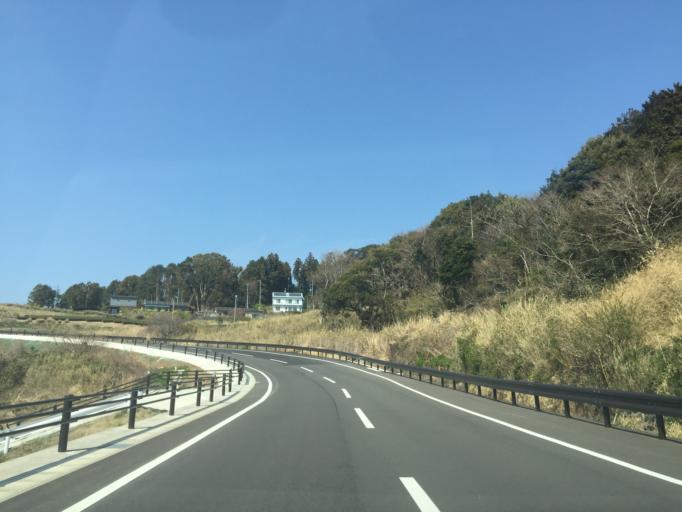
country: JP
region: Shizuoka
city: Kanaya
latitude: 34.8062
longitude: 138.1249
